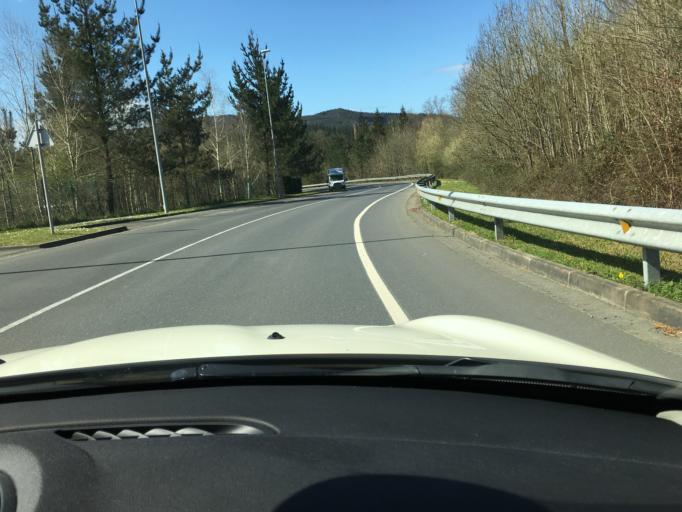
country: ES
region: Basque Country
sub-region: Bizkaia
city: Amorebieta
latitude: 43.2360
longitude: -2.7520
